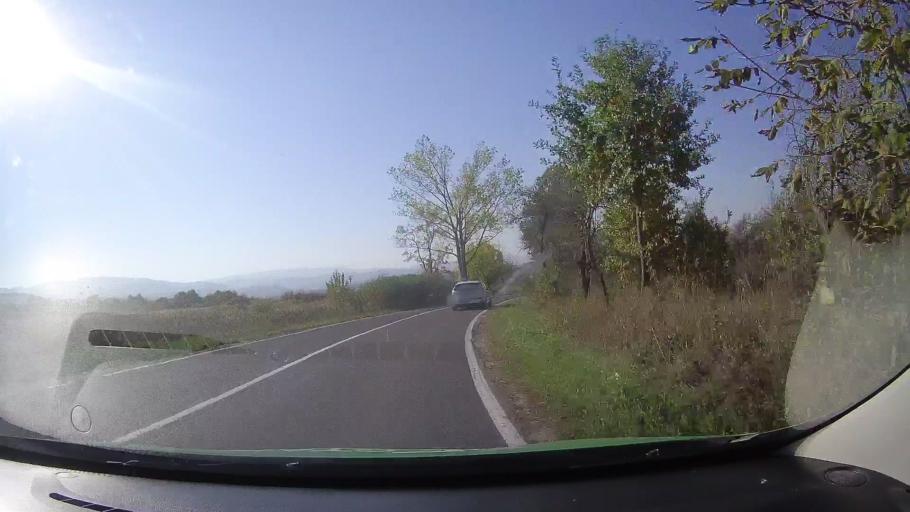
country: RO
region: Timis
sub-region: Comuna Curtea
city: Curtea
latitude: 45.8466
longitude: 22.3138
